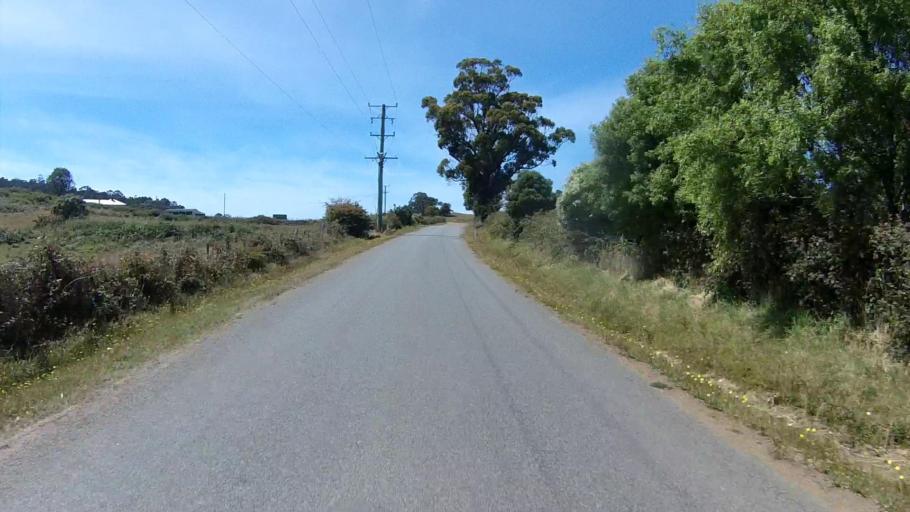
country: AU
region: Tasmania
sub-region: Sorell
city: Sorell
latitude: -42.7057
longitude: 147.7446
